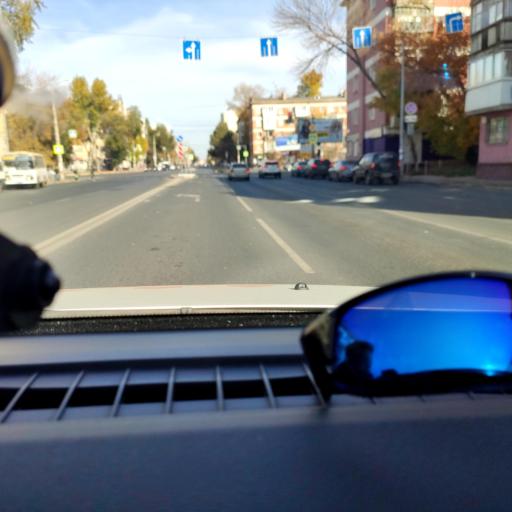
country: RU
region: Samara
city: Samara
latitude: 53.1998
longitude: 50.1903
